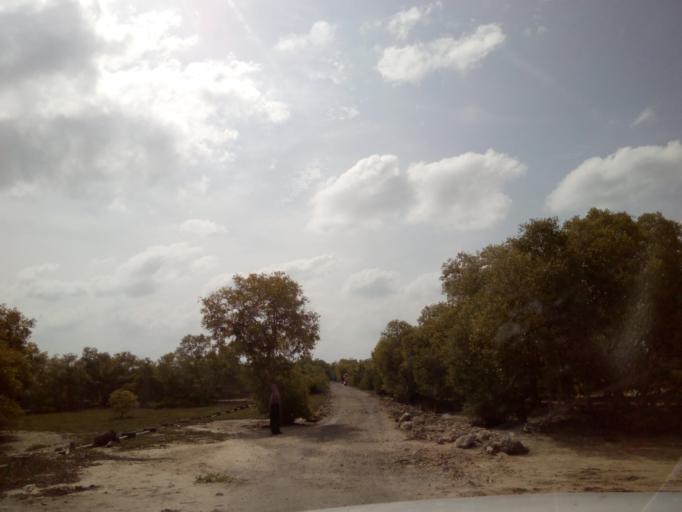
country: TZ
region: Zanzibar Central/South
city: Mahonda
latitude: -6.3103
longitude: 39.3786
